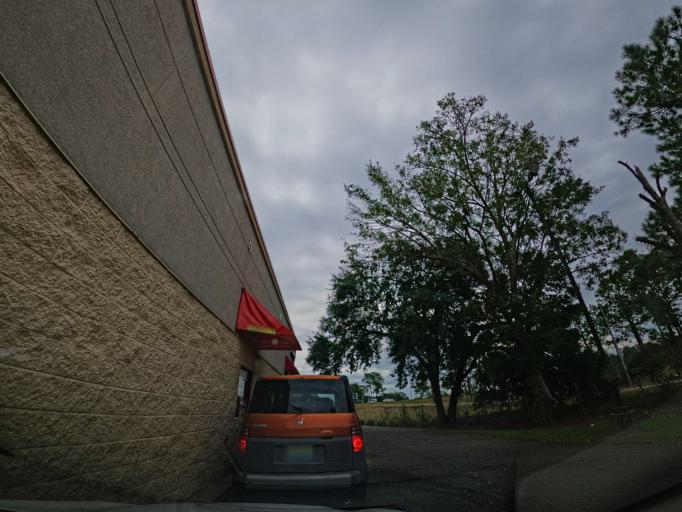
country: US
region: Alabama
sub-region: Mobile County
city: Grand Bay
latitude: 30.4973
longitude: -88.3367
